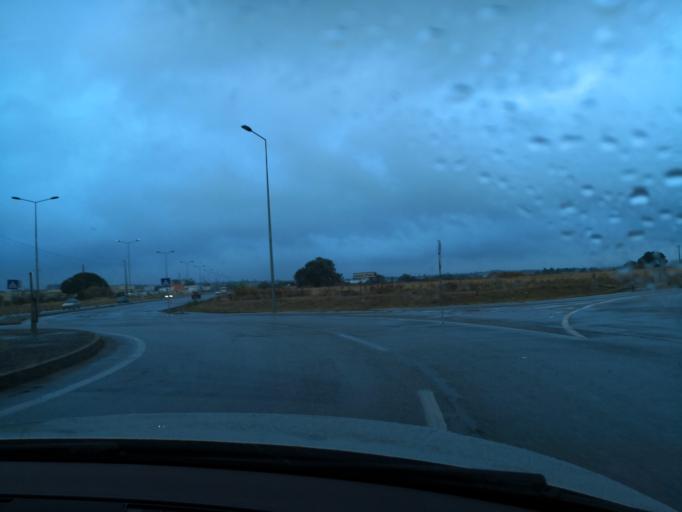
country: PT
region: Setubal
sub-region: Moita
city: Alhos Vedros
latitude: 38.6522
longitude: -9.0128
